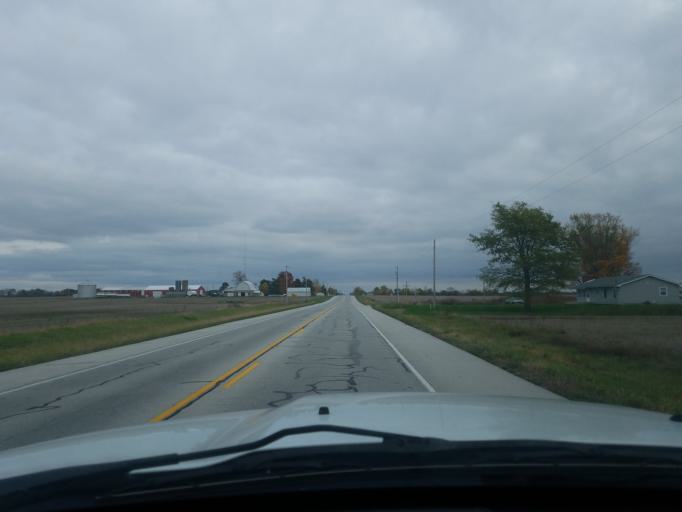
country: US
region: Indiana
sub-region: Johnson County
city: Franklin
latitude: 39.4953
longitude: -85.9298
